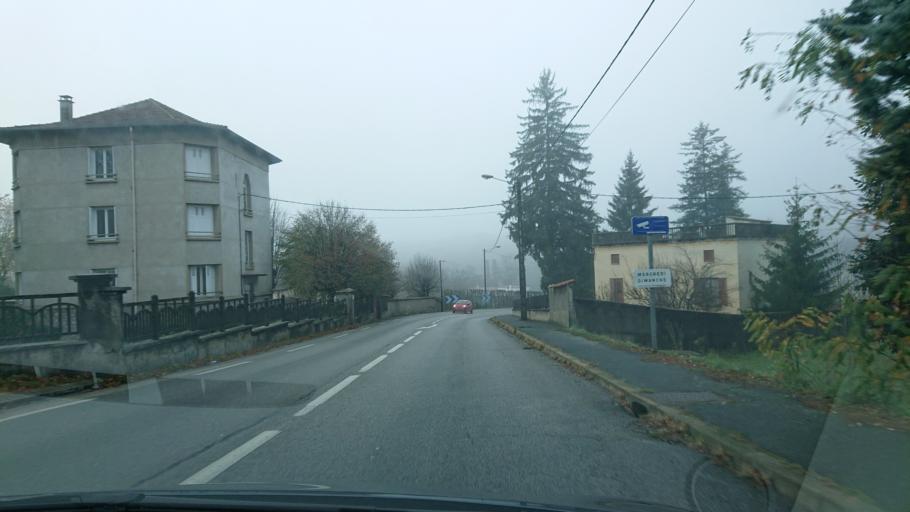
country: FR
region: Auvergne
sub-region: Departement de la Haute-Loire
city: Bas-en-Basset
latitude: 45.2966
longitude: 4.1206
